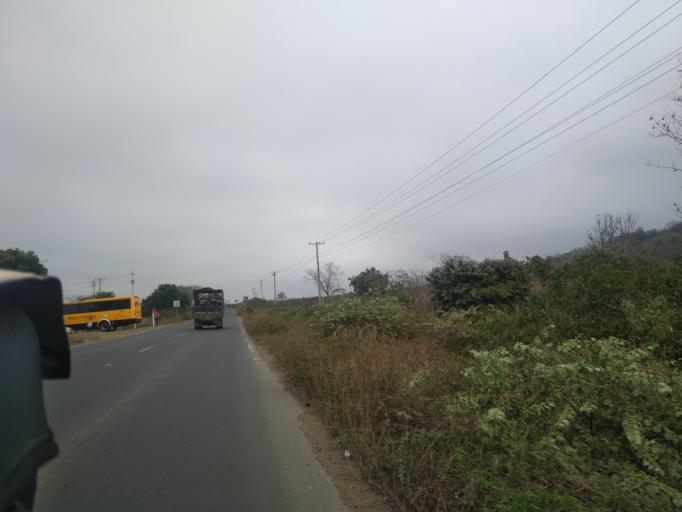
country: EC
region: Manabi
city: Montecristi
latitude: -1.0628
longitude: -80.6560
